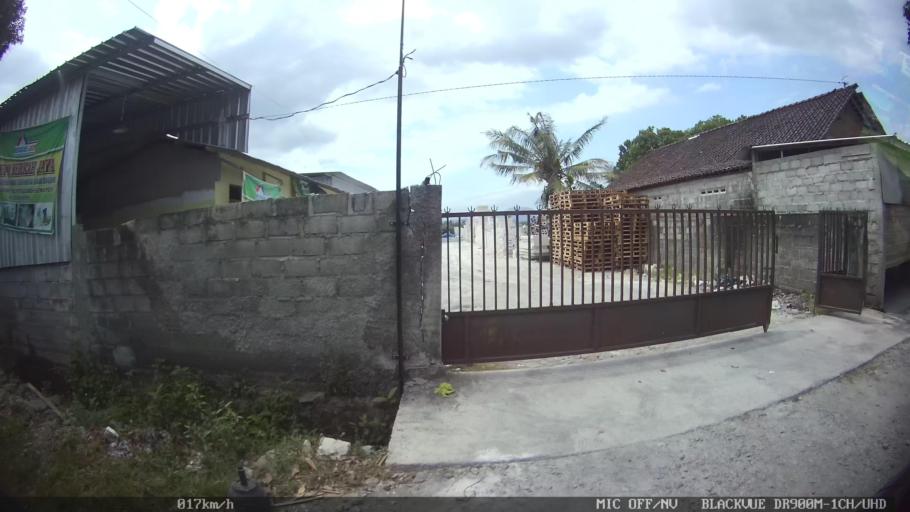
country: ID
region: Daerah Istimewa Yogyakarta
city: Depok
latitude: -7.8082
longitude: 110.4433
